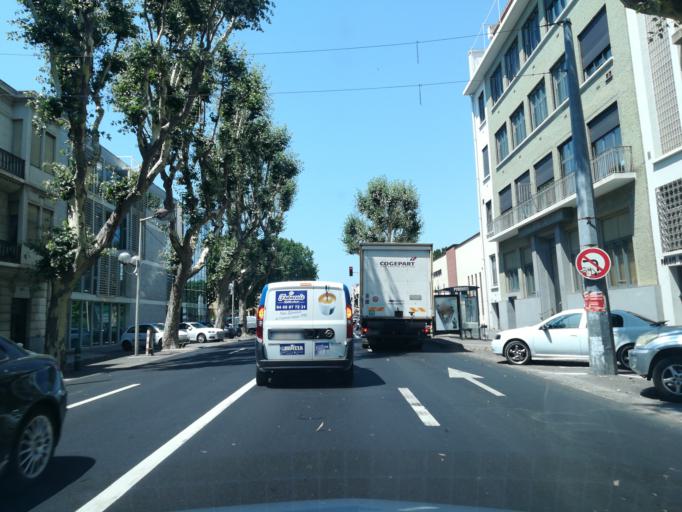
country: FR
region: Languedoc-Roussillon
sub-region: Departement des Pyrenees-Orientales
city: Perpignan
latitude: 42.6962
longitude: 2.8884
